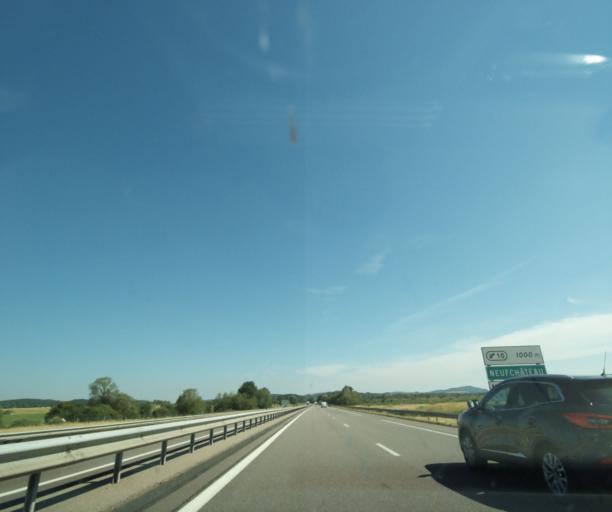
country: FR
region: Lorraine
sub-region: Departement des Vosges
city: Chatenois
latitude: 48.2884
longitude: 5.8559
